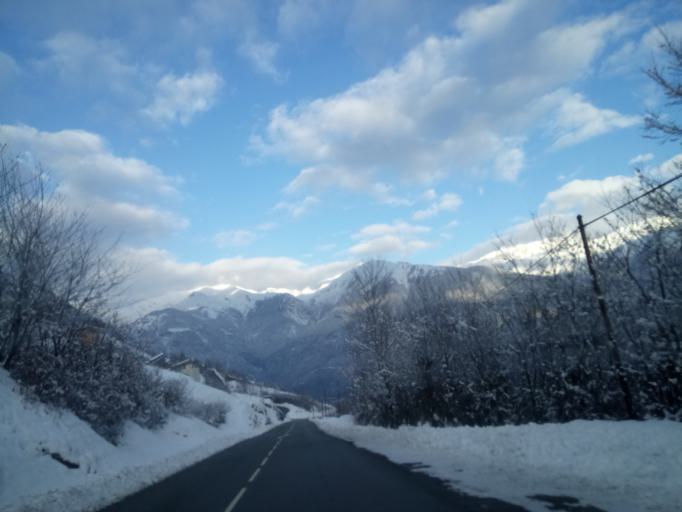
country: FR
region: Rhone-Alpes
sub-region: Departement de la Savoie
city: Saint-Jean-de-Maurienne
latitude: 45.2584
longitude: 6.3217
